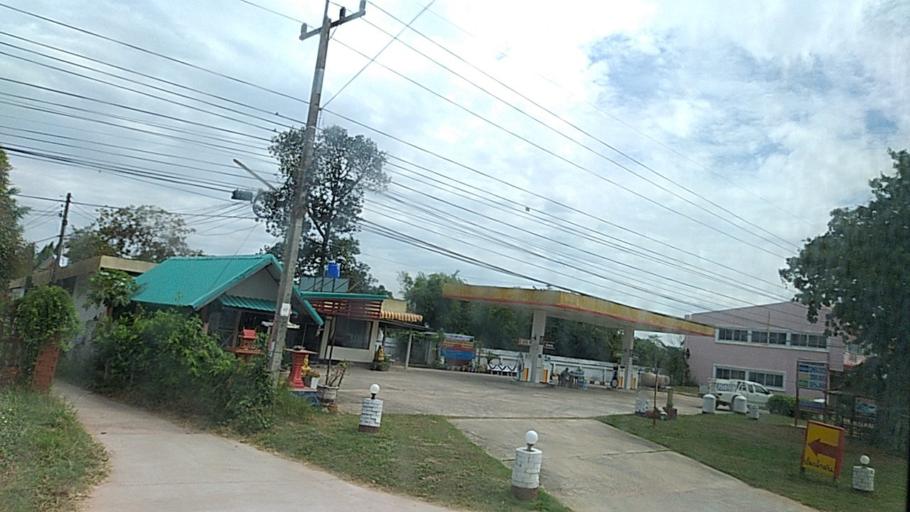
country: TH
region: Maha Sarakham
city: Chiang Yuen
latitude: 16.3517
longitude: 103.1186
